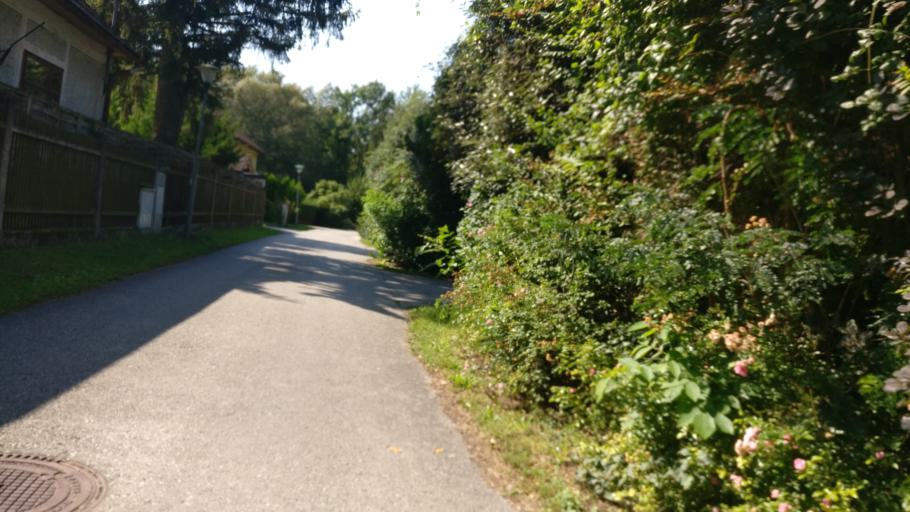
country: AT
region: Lower Austria
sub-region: Politischer Bezirk Baden
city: Mitterndorf an der Fischa
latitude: 47.9781
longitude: 16.4447
